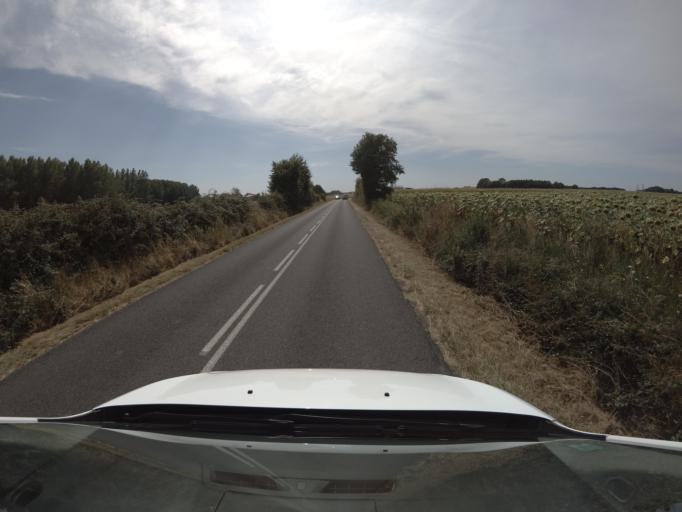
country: FR
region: Poitou-Charentes
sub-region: Departement des Deux-Sevres
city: Saint-Leger-de-Montbrun
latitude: 46.9995
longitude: -0.1035
